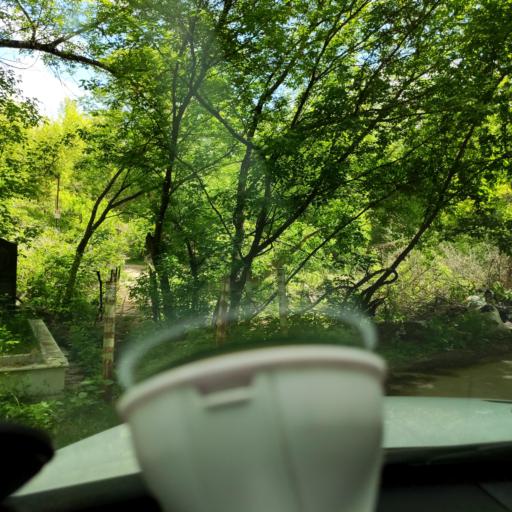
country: RU
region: Samara
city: Petra-Dubrava
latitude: 53.2765
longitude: 50.3230
